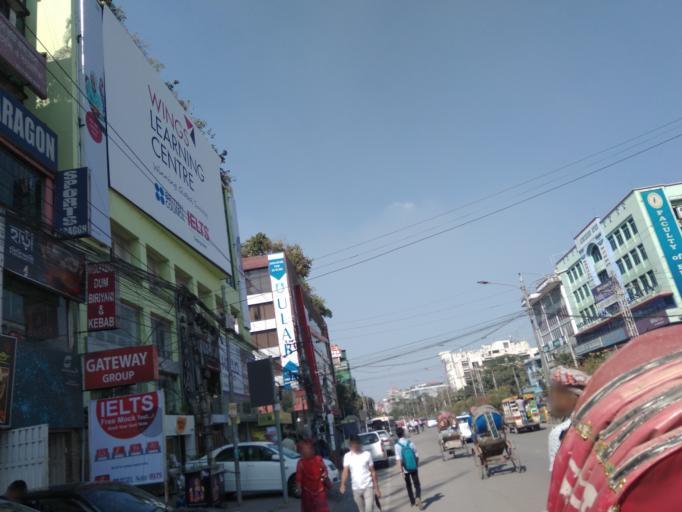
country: BD
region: Dhaka
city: Azimpur
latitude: 23.7403
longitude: 90.3749
